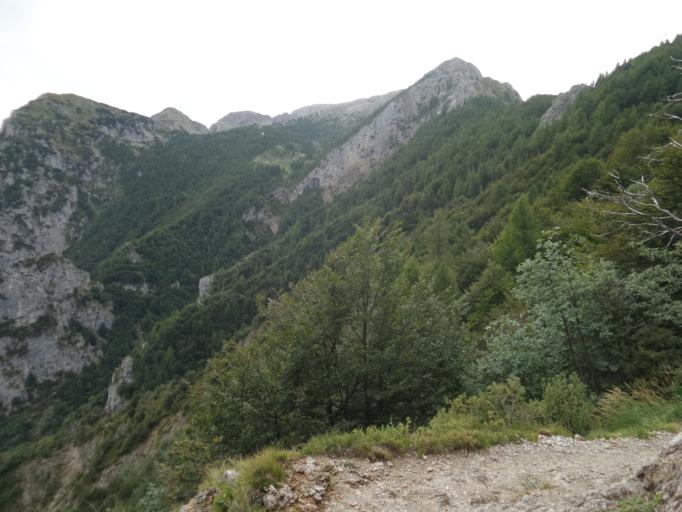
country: IT
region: Lombardy
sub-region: Provincia di Lecco
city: Esino Lario
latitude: 45.9742
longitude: 9.3601
